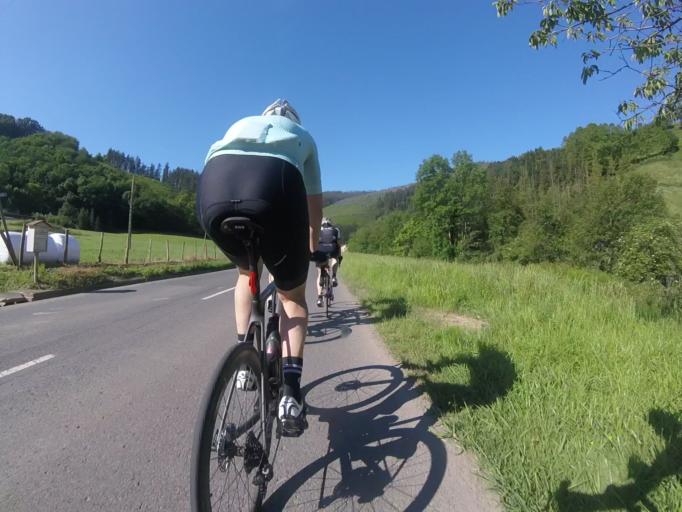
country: ES
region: Basque Country
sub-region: Provincia de Guipuzcoa
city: Beizama
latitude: 43.1442
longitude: -2.2337
